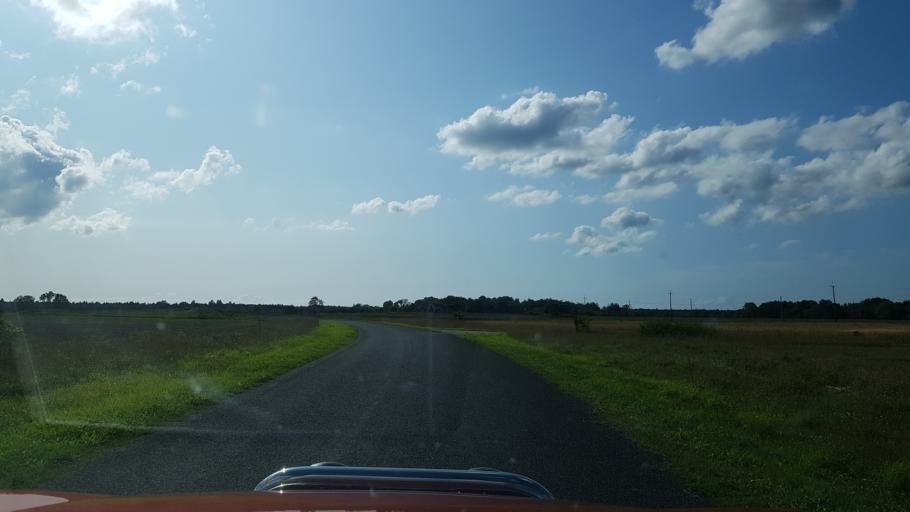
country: EE
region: Harju
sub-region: Paldiski linn
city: Paldiski
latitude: 59.1992
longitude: 23.9528
